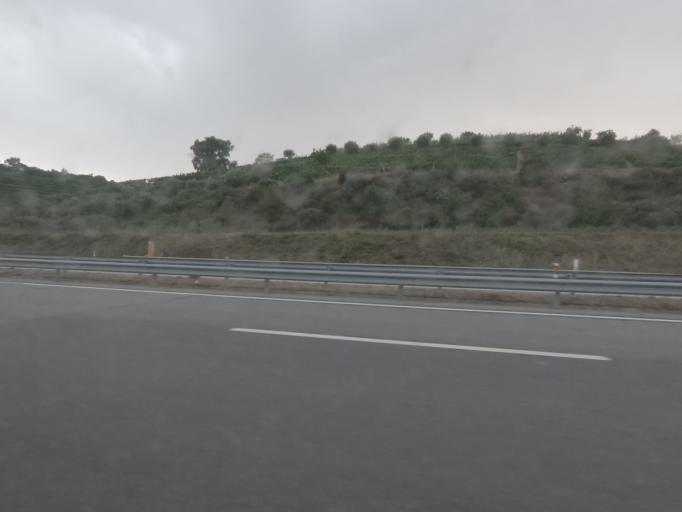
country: PT
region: Vila Real
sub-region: Santa Marta de Penaguiao
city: Santa Marta de Penaguiao
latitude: 41.2138
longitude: -7.7348
